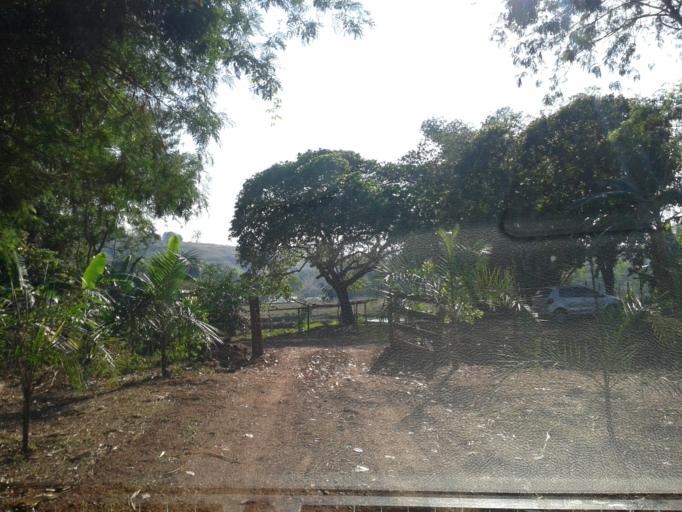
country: BR
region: Minas Gerais
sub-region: Ituiutaba
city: Ituiutaba
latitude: -18.9445
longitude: -49.4589
